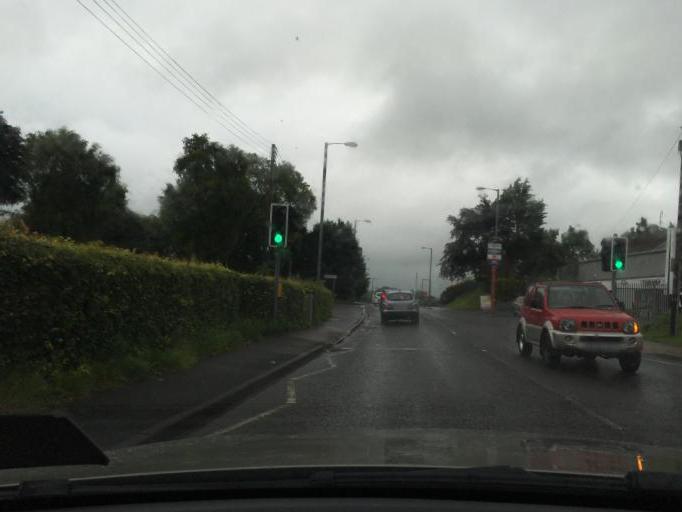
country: GB
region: Northern Ireland
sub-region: Fermanagh District
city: Enniskillen
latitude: 54.3529
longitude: -7.6365
